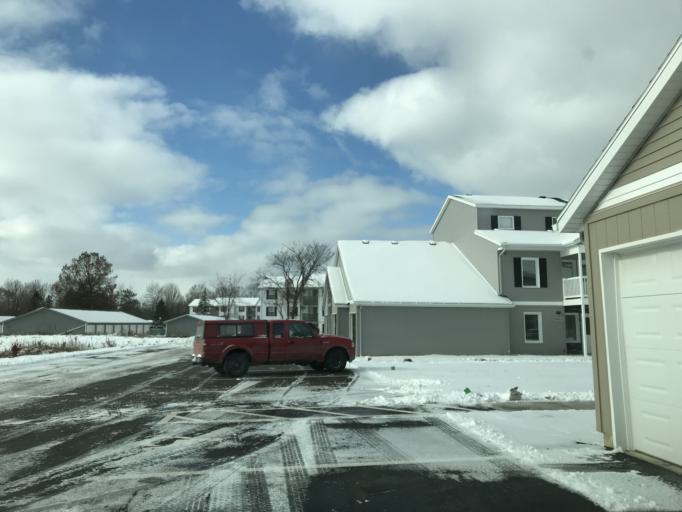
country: US
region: Michigan
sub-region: Kent County
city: Kentwood
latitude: 42.8514
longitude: -85.6474
